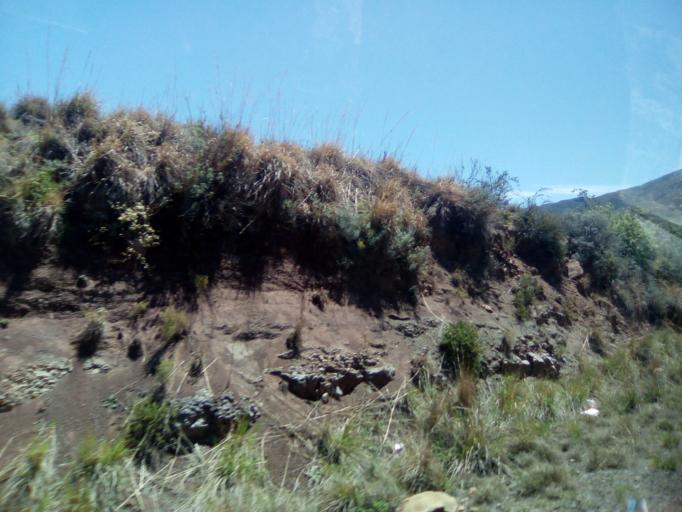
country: LS
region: Qacha's Nek
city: Qacha's Nek
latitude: -30.1075
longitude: 28.6642
